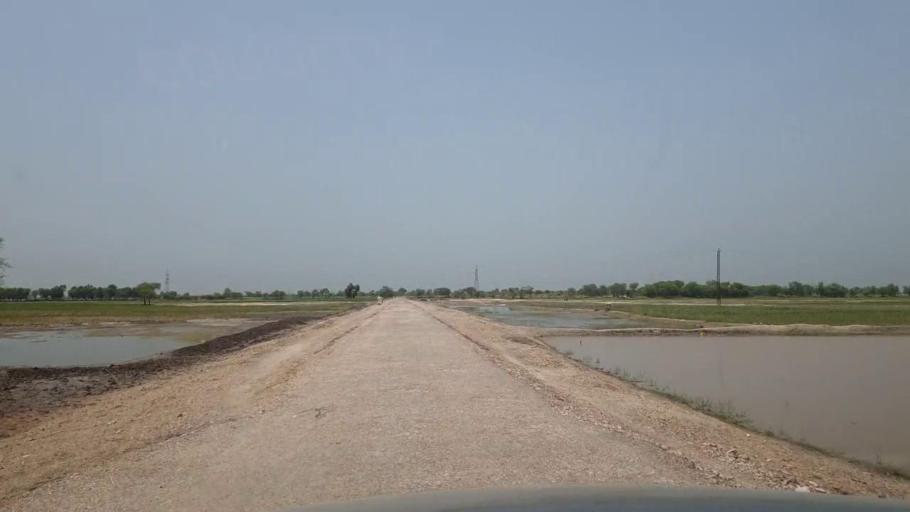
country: PK
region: Sindh
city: Garhi Yasin
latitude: 27.8704
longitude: 68.4521
